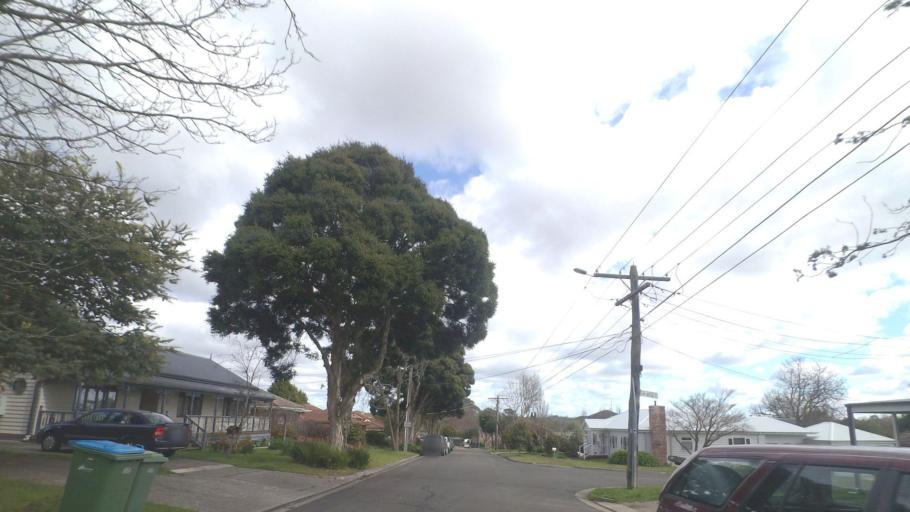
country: AU
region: Victoria
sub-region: Maroondah
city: Heathmont
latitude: -37.8315
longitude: 145.2362
